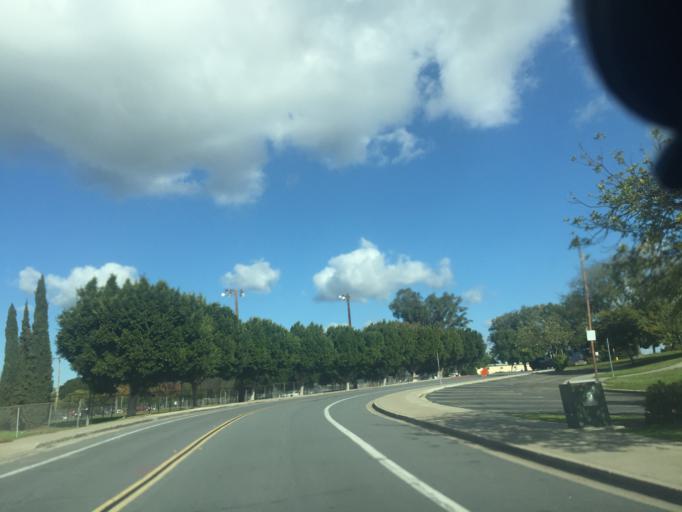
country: US
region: California
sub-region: San Diego County
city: La Mesa
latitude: 32.7937
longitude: -117.0818
